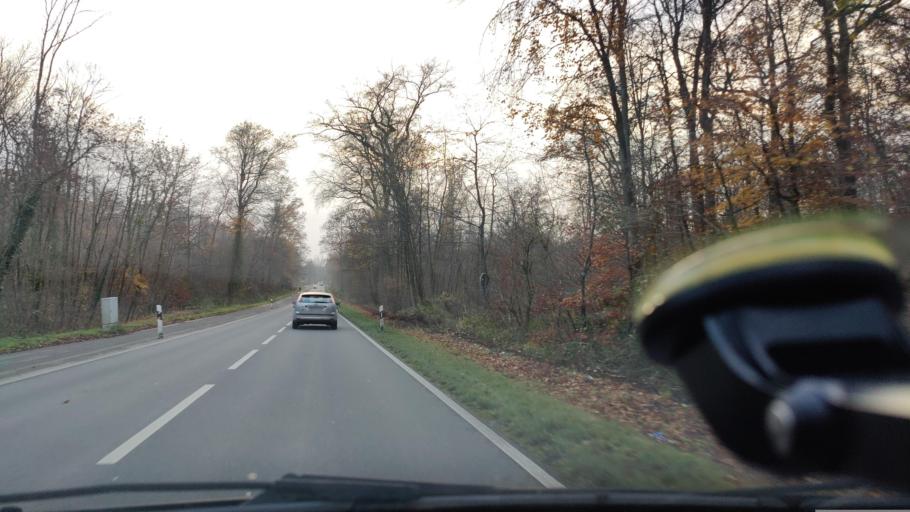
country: DE
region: North Rhine-Westphalia
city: Lunen
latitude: 51.6432
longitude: 7.5321
